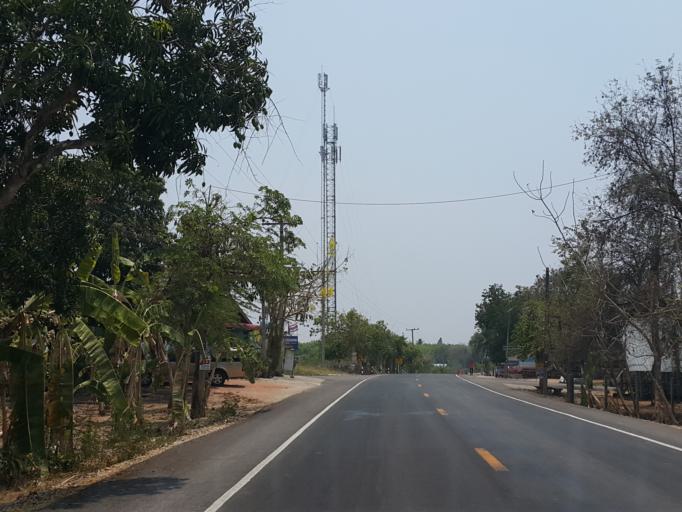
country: TH
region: Kamphaeng Phet
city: Pang Sila Thong
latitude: 16.0323
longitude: 99.3732
